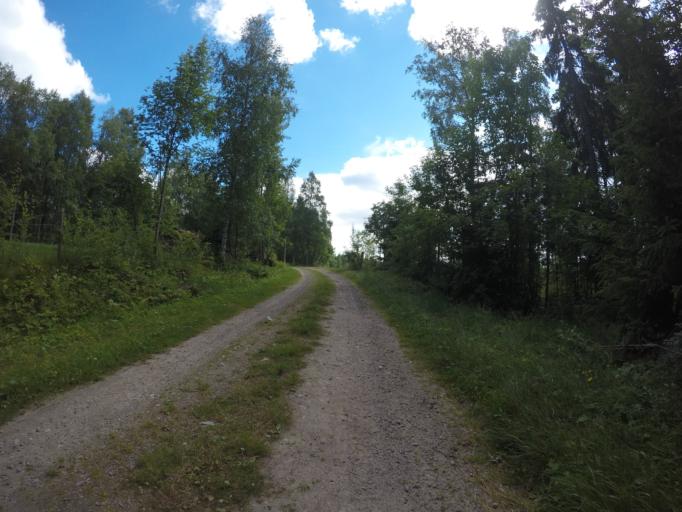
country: SE
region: Vaermland
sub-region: Filipstads Kommun
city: Lesjofors
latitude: 60.0684
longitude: 14.4609
